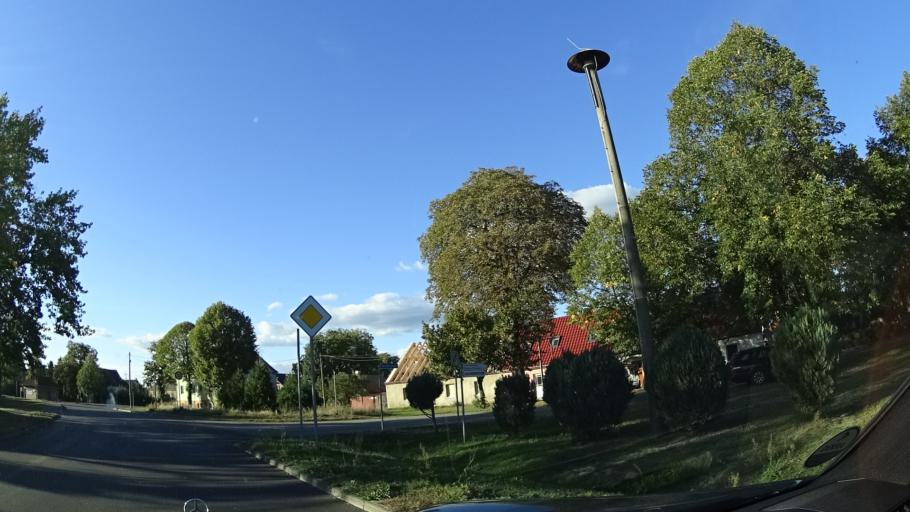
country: DE
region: Brandenburg
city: Dabergotz
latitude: 52.9284
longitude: 12.7458
